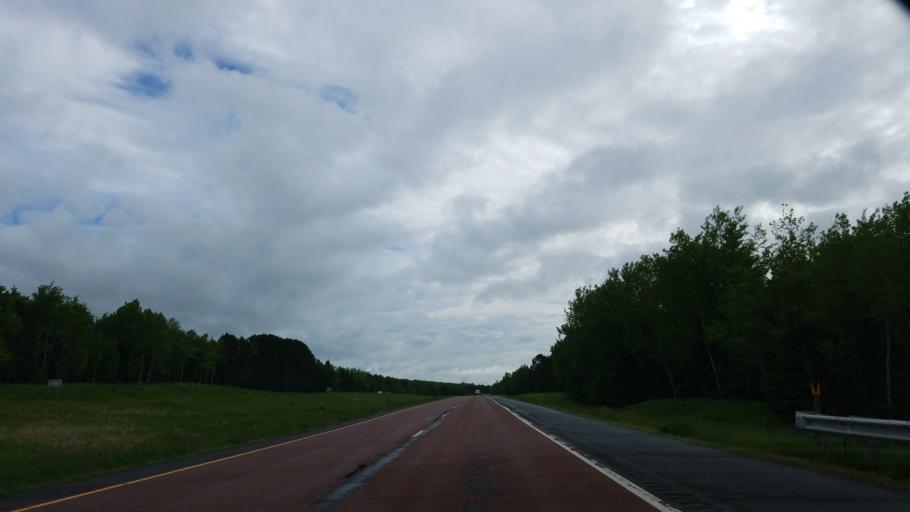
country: US
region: Minnesota
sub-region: Saint Louis County
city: Arnold
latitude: 46.9018
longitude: -91.8985
